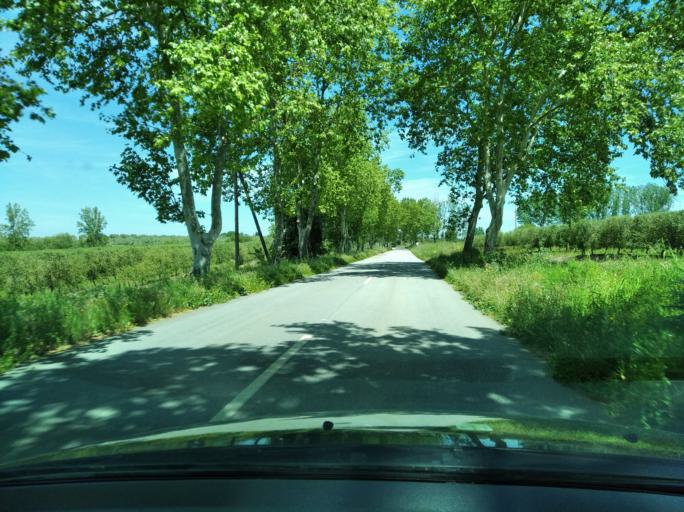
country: PT
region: Portalegre
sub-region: Avis
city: Avis
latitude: 39.0827
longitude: -7.8797
